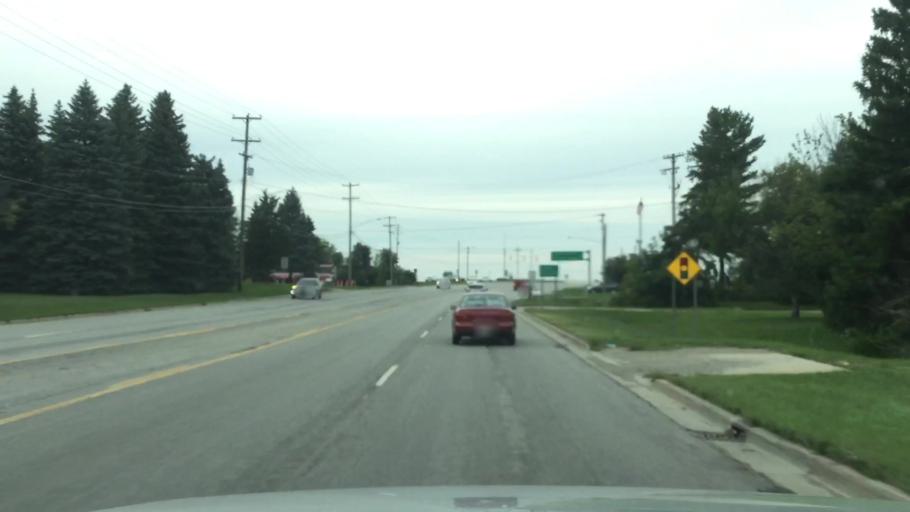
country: US
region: Michigan
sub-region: Genesee County
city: Grand Blanc
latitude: 42.8926
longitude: -83.6318
